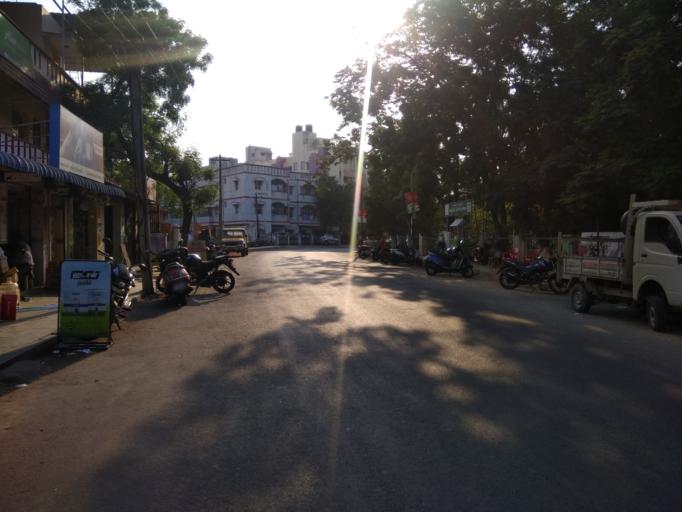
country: IN
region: Tamil Nadu
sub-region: Kancheepuram
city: Madipakkam
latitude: 12.9808
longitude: 80.1861
